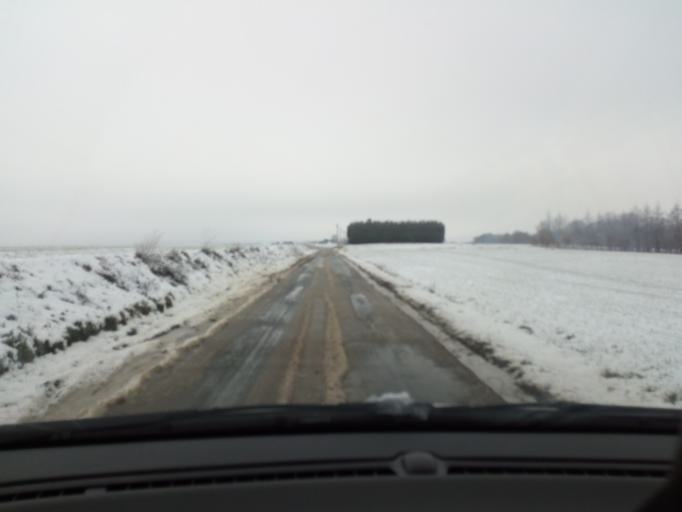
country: FR
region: Nord-Pas-de-Calais
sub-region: Departement du Nord
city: Boussois
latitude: 50.3575
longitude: 4.0256
